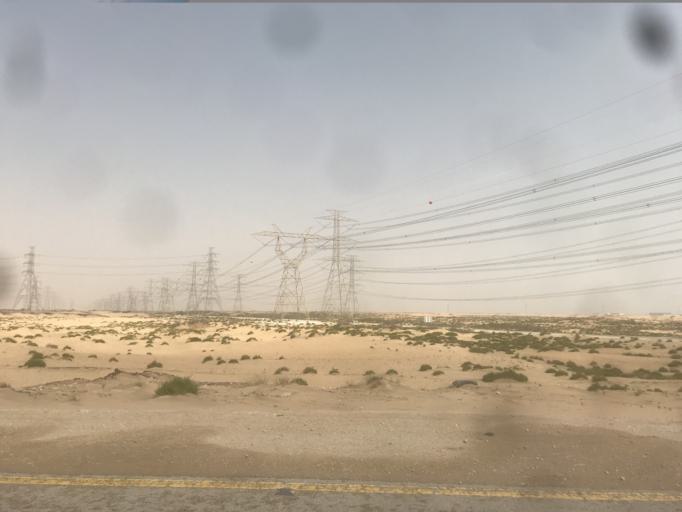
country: SA
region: Eastern Province
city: Abqaiq
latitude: 25.9065
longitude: 49.9088
